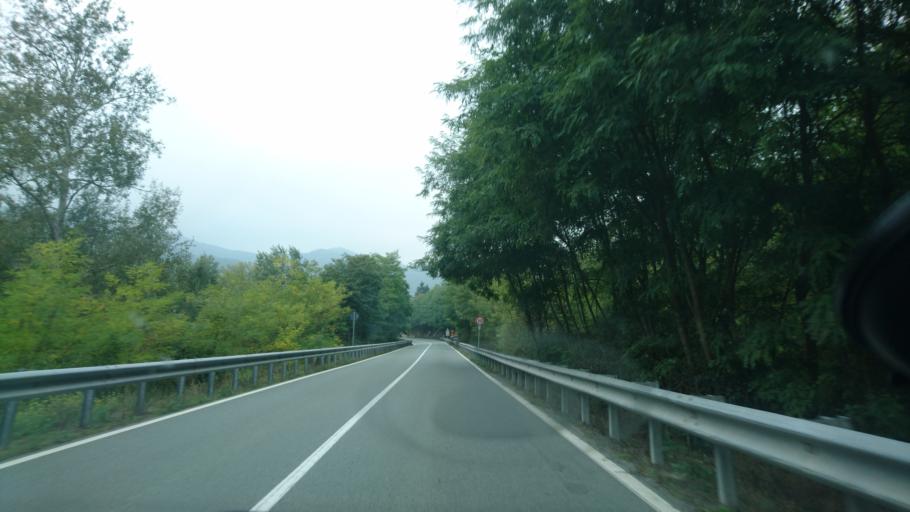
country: IT
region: Piedmont
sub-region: Provincia di Alessandria
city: Ponti
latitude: 44.6112
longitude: 8.3535
